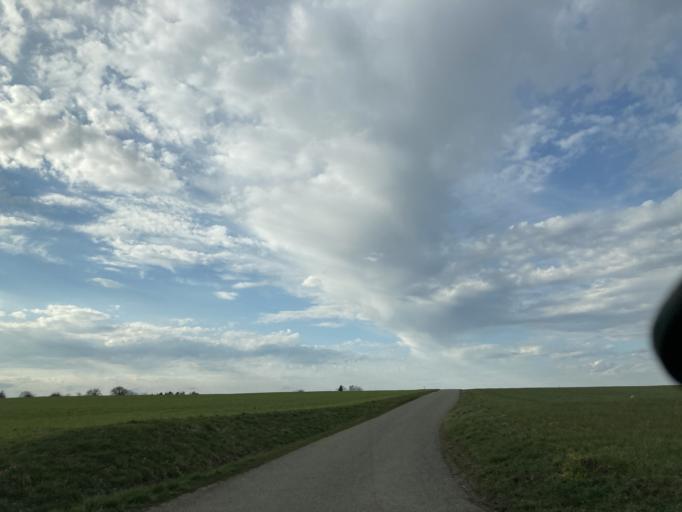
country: DE
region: Baden-Wuerttemberg
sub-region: Tuebingen Region
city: Nehren
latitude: 48.4395
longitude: 9.0700
